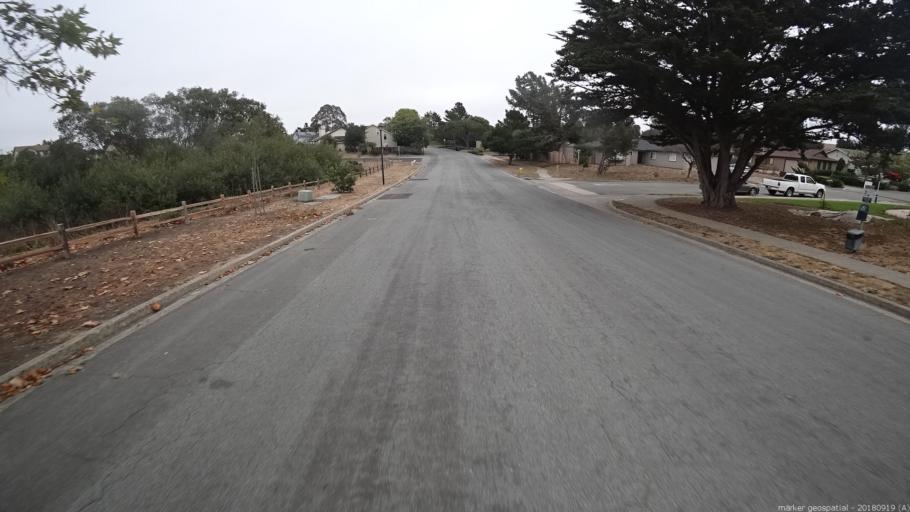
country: US
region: California
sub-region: Monterey County
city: Castroville
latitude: 36.7749
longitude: -121.7264
